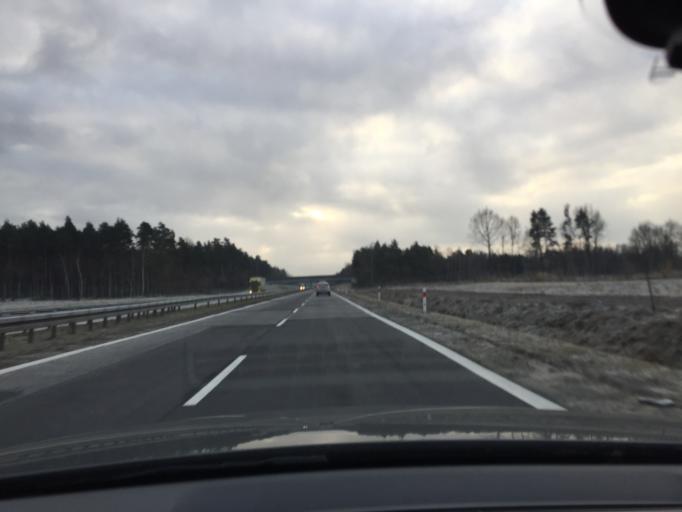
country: PL
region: Lubusz
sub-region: Powiat zarski
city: Lipinki Luzyckie
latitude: 51.5794
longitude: 15.0267
